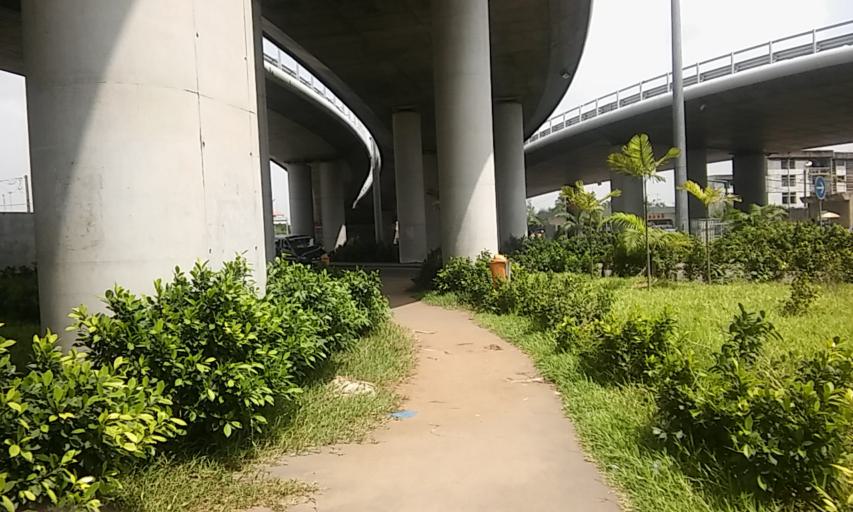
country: CI
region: Lagunes
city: Abidjan
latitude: 5.2965
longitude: -3.9816
